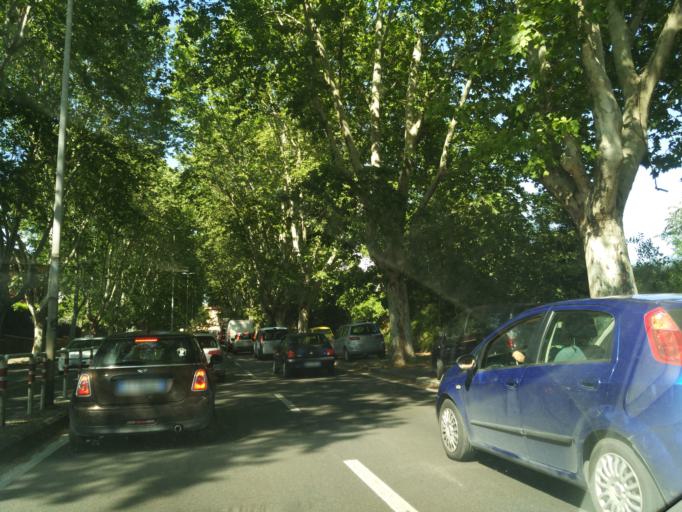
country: IT
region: Latium
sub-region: Citta metropolitana di Roma Capitale
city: Rome
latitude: 41.8720
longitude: 12.5043
